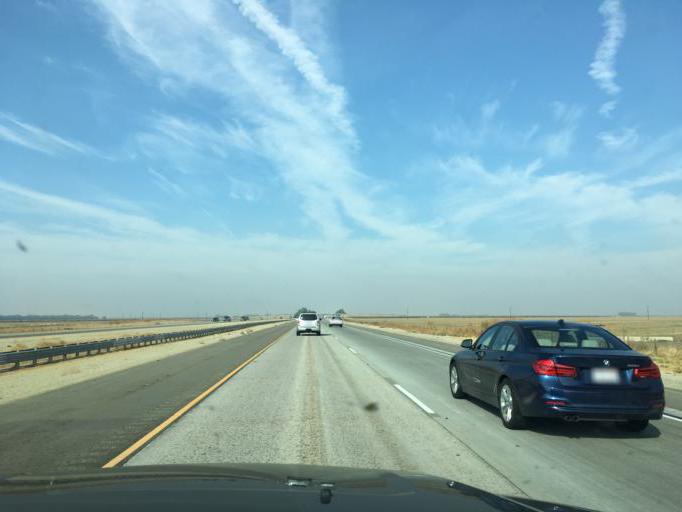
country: US
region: California
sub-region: Kern County
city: Lost Hills
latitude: 35.5674
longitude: -119.6080
